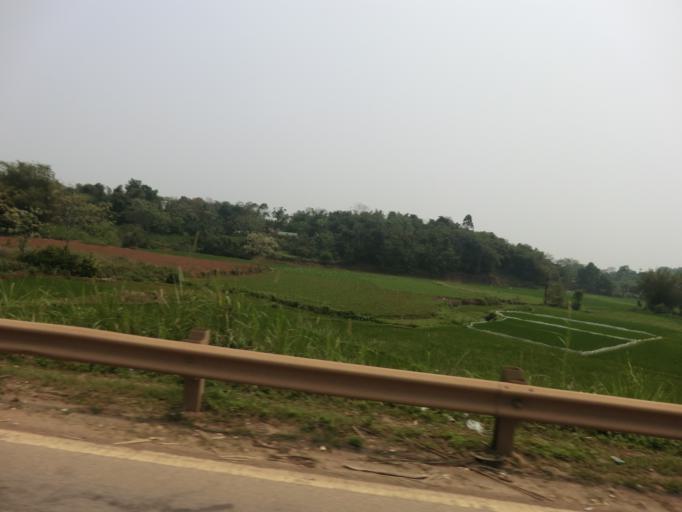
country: VN
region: Thanh Hoa
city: Thi Tran Ngoc Lac
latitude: 20.0105
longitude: 105.3957
